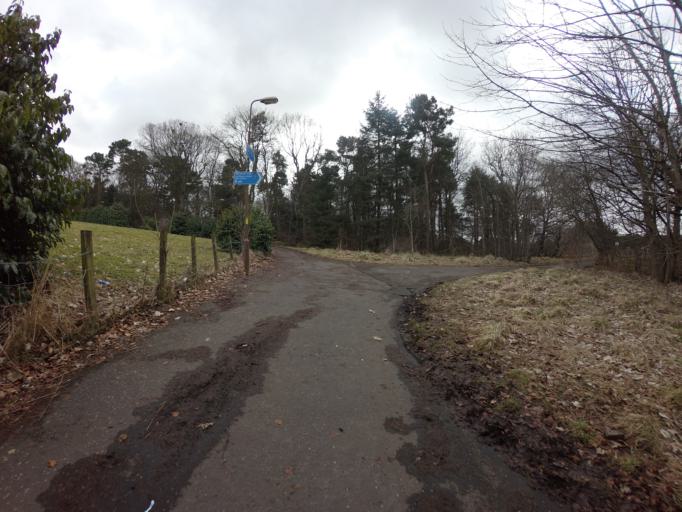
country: GB
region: Scotland
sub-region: West Lothian
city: Livingston
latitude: 55.8781
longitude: -3.5167
